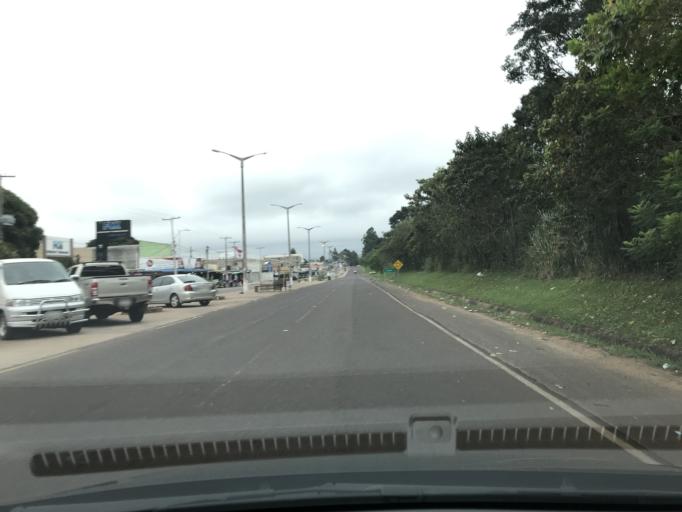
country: PY
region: Canindeyu
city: Salto del Guaira
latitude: -24.0498
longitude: -54.3064
